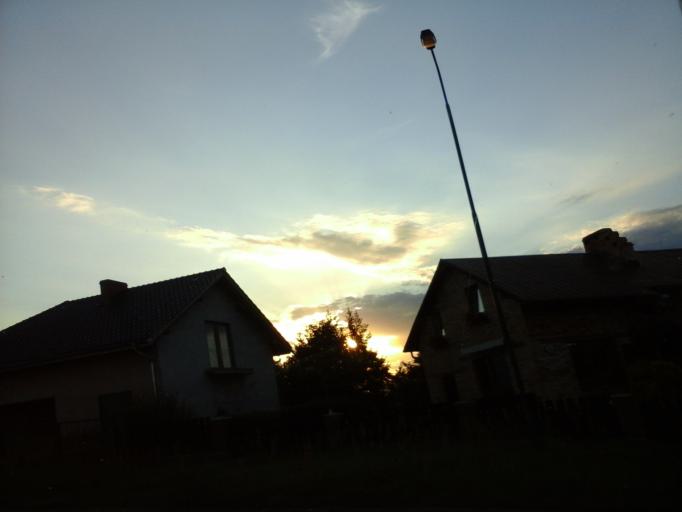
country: PL
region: West Pomeranian Voivodeship
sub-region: Powiat choszczenski
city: Choszczno
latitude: 53.1810
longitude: 15.4147
